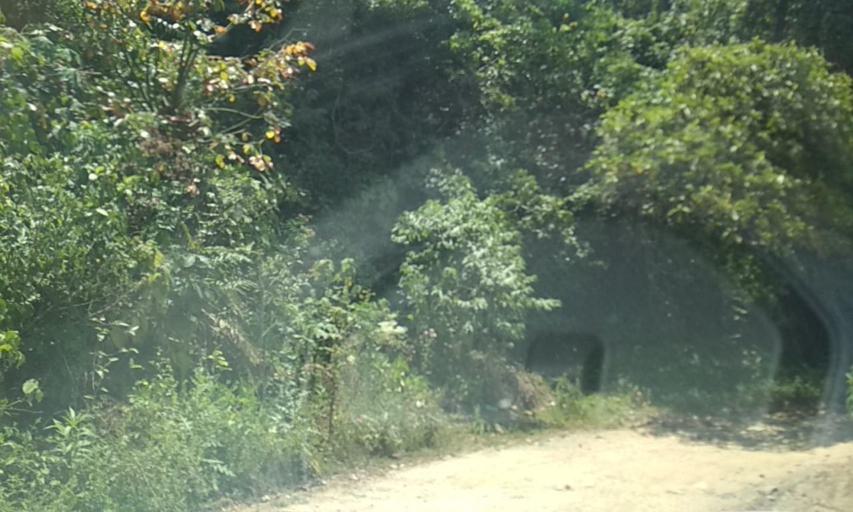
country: MX
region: Chiapas
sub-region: Tecpatan
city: Raudales Malpaso
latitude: 17.3949
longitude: -93.7245
